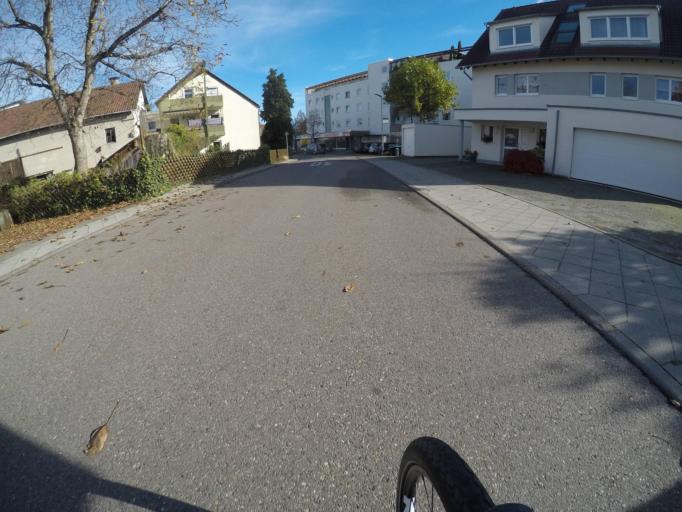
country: DE
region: Baden-Wuerttemberg
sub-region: Regierungsbezirk Stuttgart
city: Leinfelden-Echterdingen
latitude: 48.6927
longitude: 9.1438
